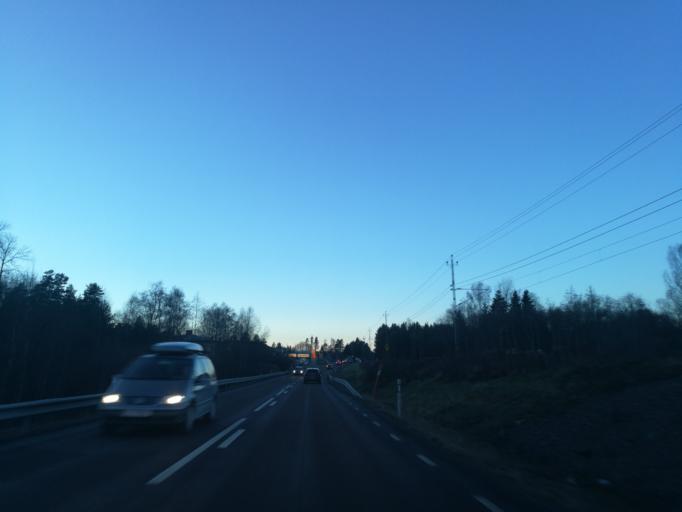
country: SE
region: Vaermland
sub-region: Eda Kommun
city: Charlottenberg
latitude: 59.9220
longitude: 12.2660
